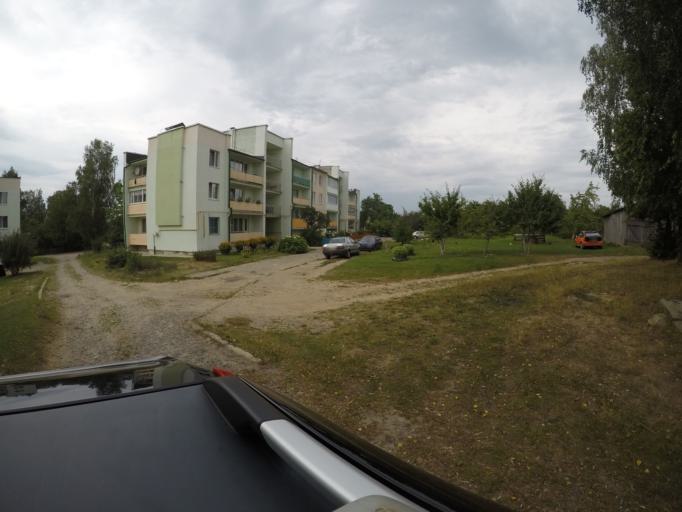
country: BY
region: Grodnenskaya
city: Hal'shany
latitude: 54.2565
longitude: 26.0186
